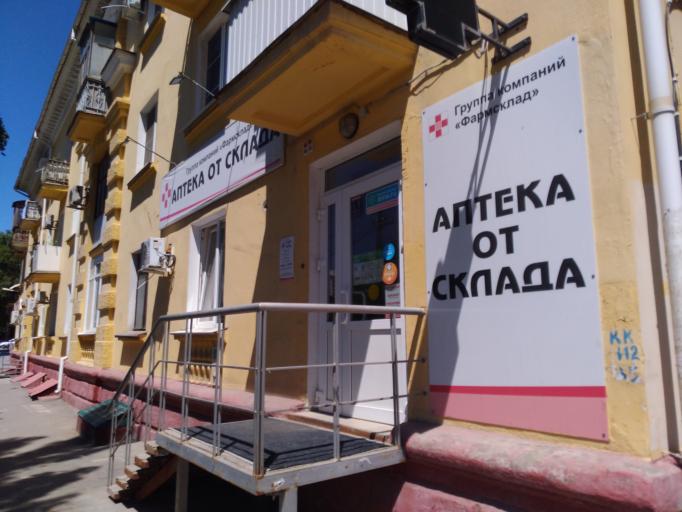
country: RU
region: Volgograd
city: Volgograd
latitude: 48.7137
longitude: 44.4988
